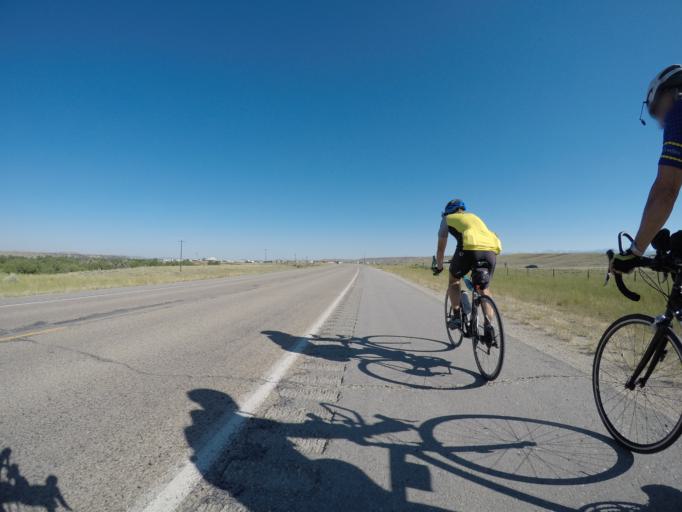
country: US
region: Wyoming
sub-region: Sublette County
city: Pinedale
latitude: 42.7569
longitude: -109.7314
